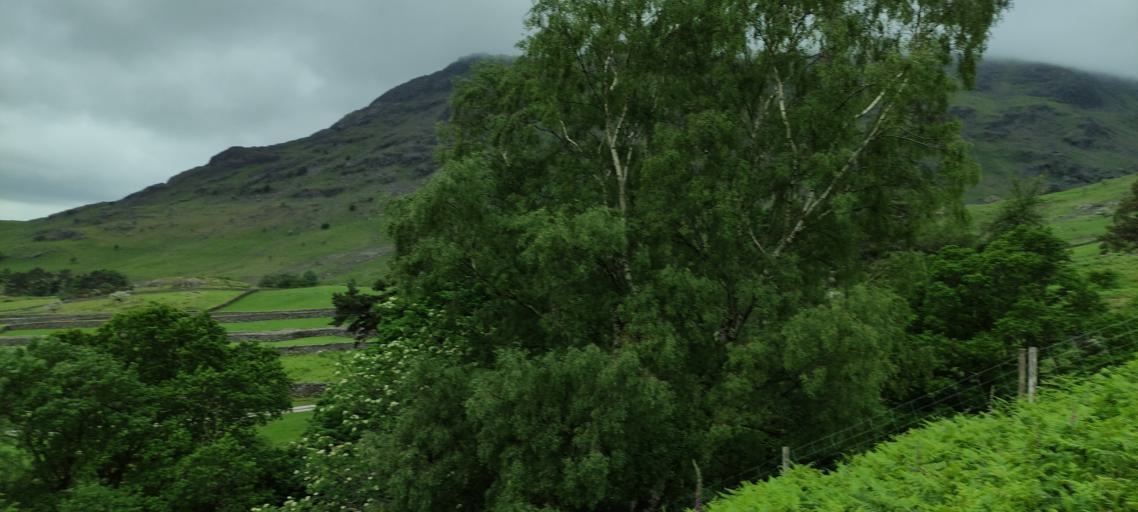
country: GB
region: England
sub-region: Cumbria
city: Seascale
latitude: 54.4519
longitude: -3.2869
